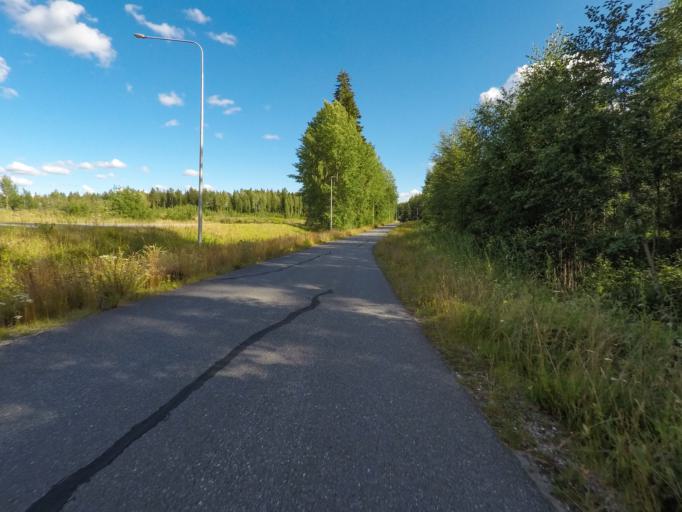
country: FI
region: South Karelia
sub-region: Lappeenranta
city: Lappeenranta
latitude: 61.0962
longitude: 28.1369
